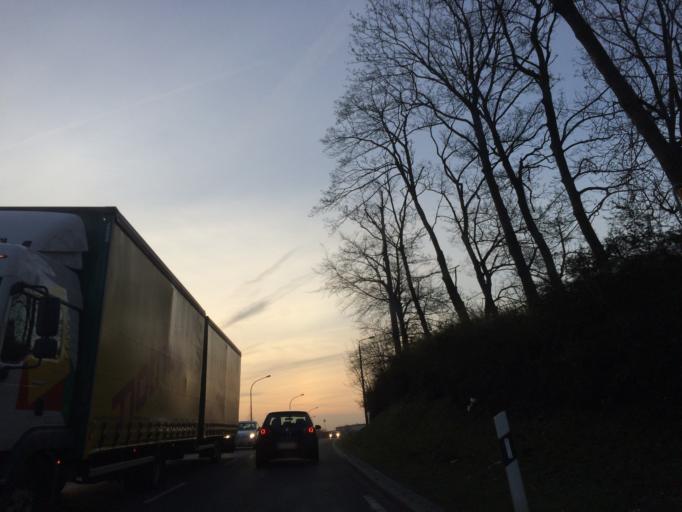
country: DE
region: Thuringia
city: Eisenberg
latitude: 50.9713
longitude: 11.8717
